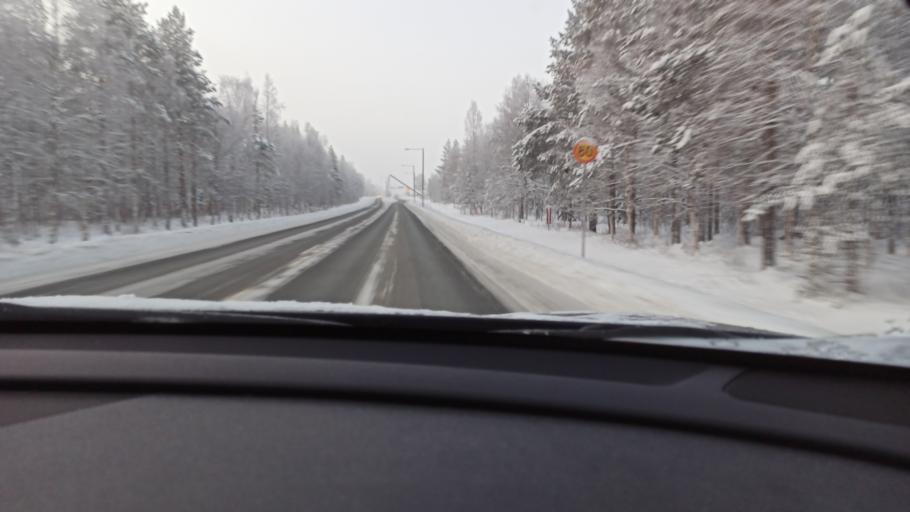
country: FI
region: Lapland
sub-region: Rovaniemi
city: Rovaniemi
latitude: 66.5467
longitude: 25.8608
